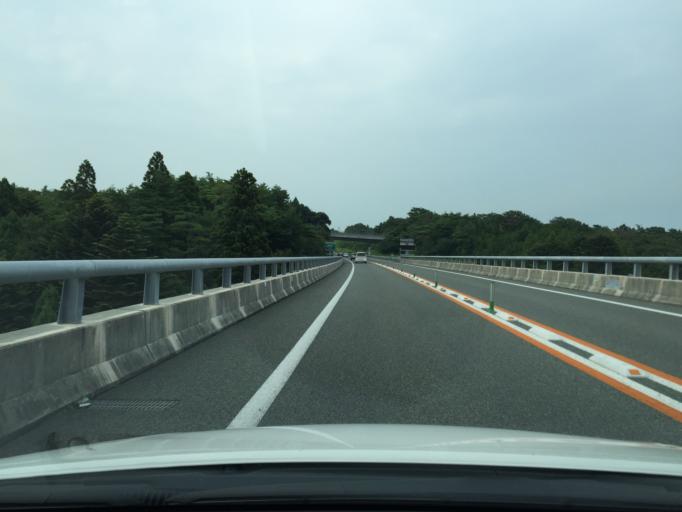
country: JP
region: Fukushima
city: Iwaki
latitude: 37.2502
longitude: 140.9900
